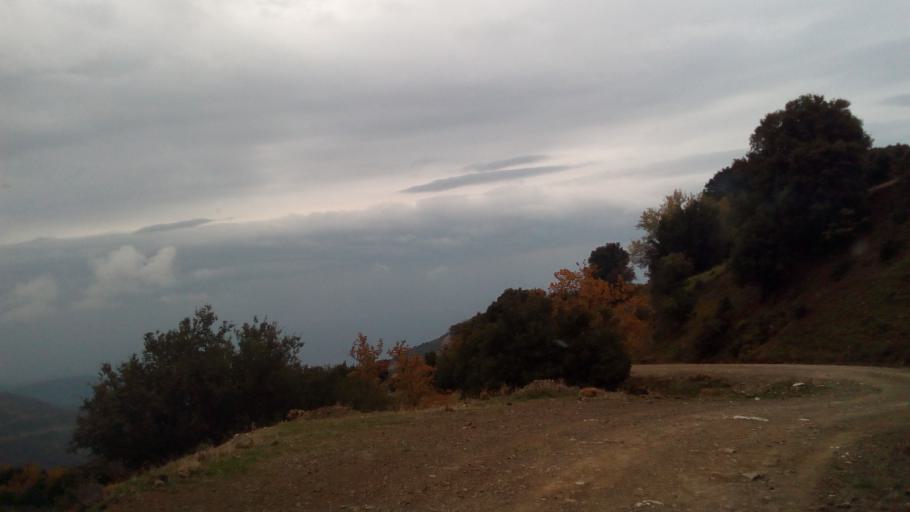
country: GR
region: West Greece
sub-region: Nomos Achaias
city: Selianitika
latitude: 38.4138
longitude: 22.0891
